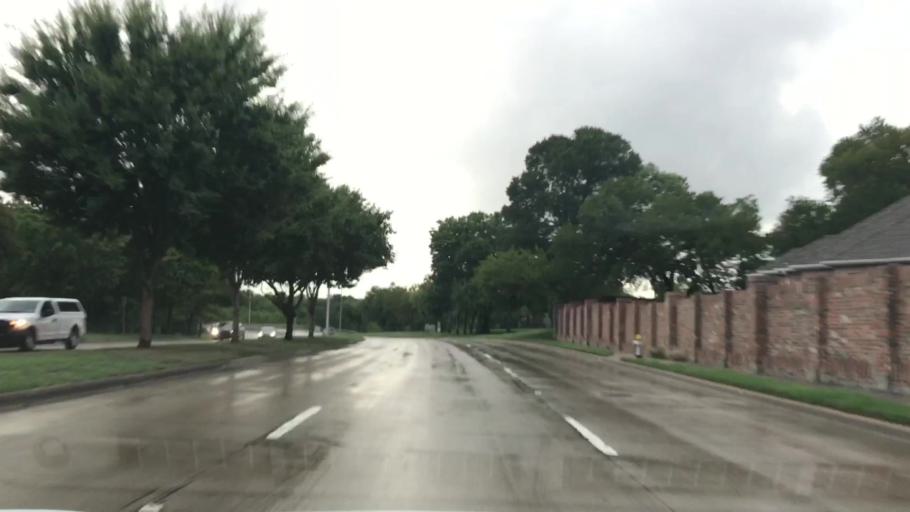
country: US
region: Texas
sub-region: Dallas County
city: Richardson
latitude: 32.8977
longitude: -96.7605
